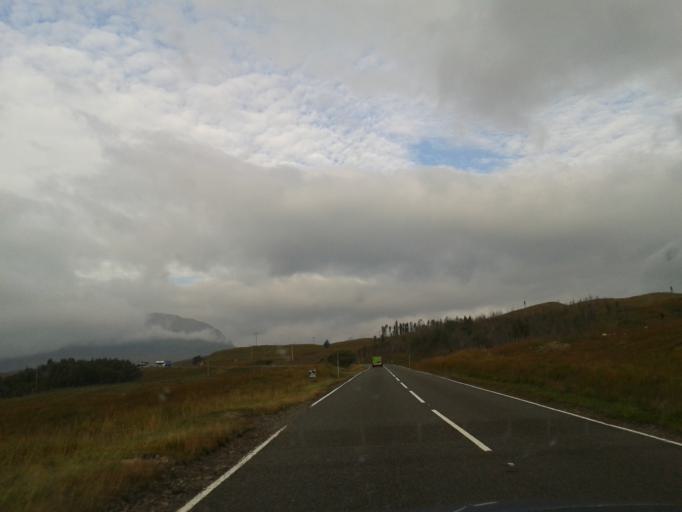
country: GB
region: Scotland
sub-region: Highland
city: Spean Bridge
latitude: 56.5674
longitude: -4.7467
